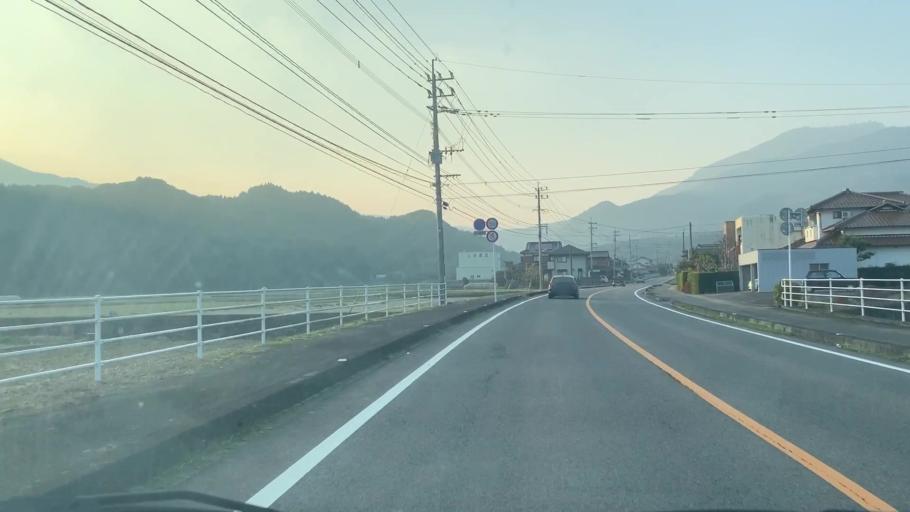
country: JP
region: Saga Prefecture
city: Takeocho-takeo
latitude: 33.2601
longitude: 130.0624
